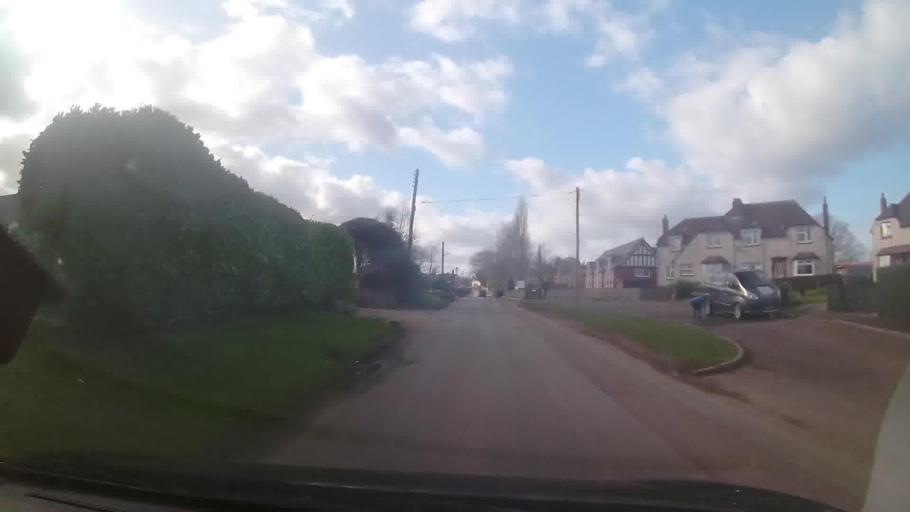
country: GB
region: England
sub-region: Shropshire
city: Whitchurch
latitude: 52.9364
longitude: -2.6784
